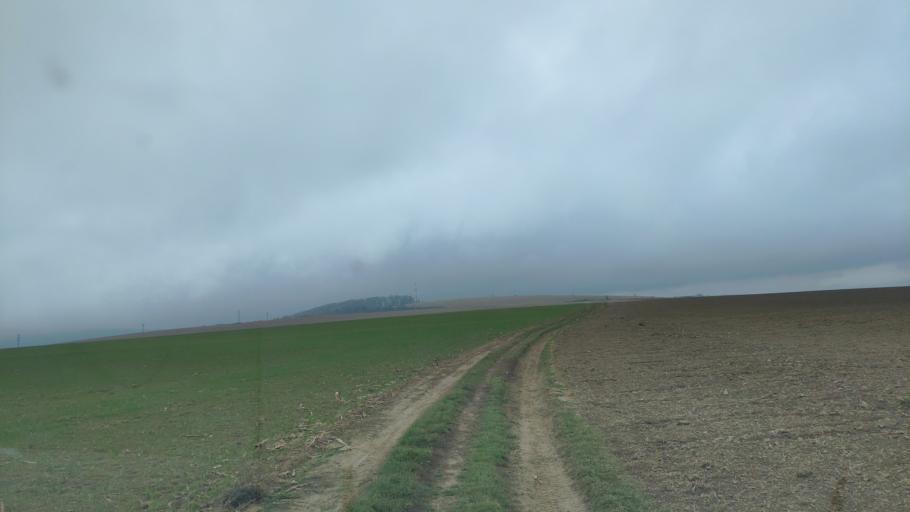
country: SK
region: Presovsky
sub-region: Okres Presov
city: Presov
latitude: 49.0131
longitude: 21.2101
